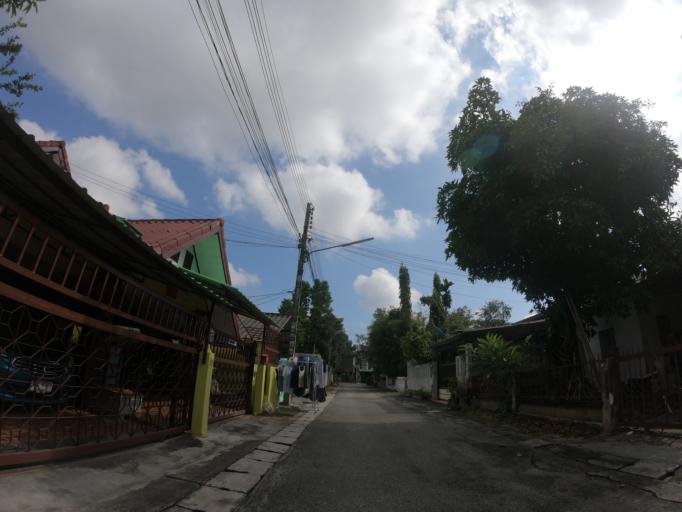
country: TH
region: Chiang Mai
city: Chiang Mai
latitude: 18.7872
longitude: 99.0316
